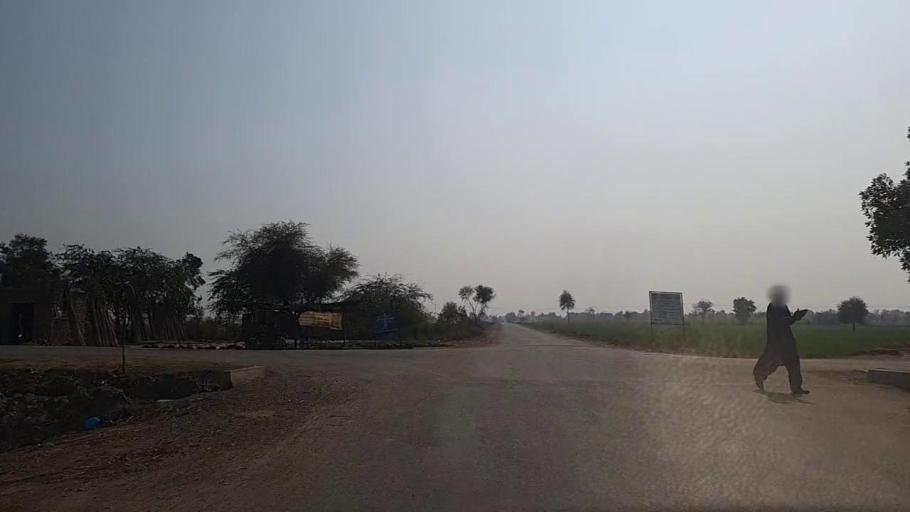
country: PK
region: Sindh
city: Jam Sahib
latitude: 26.3494
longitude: 68.5344
